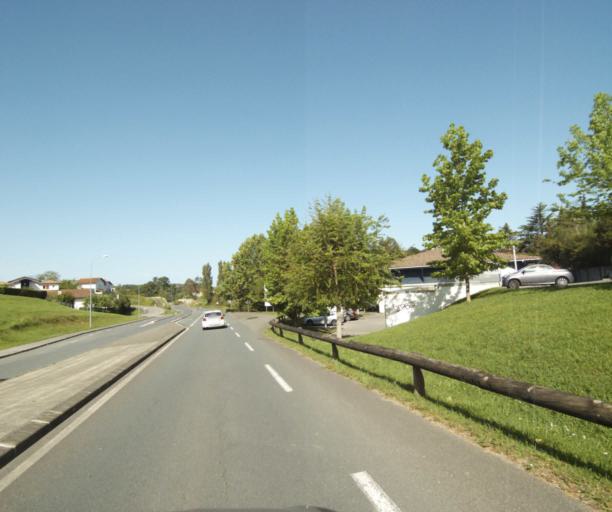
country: FR
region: Aquitaine
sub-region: Departement des Pyrenees-Atlantiques
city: Mouguerre
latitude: 43.4704
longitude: -1.4473
